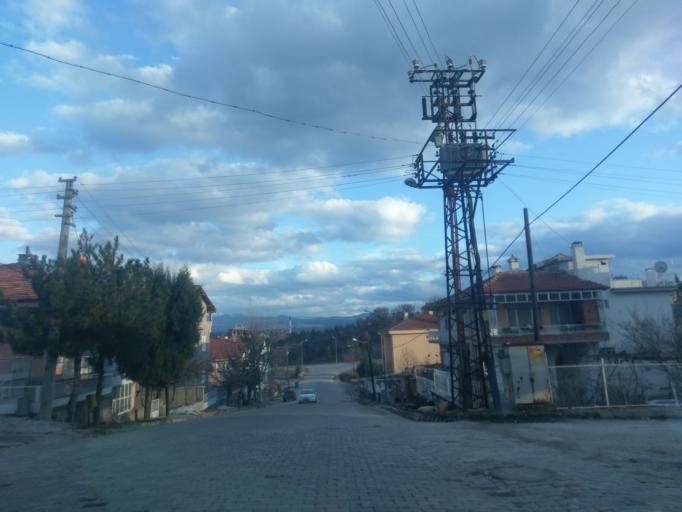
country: TR
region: Kuetahya
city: Gediz
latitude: 38.9887
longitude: 29.3858
